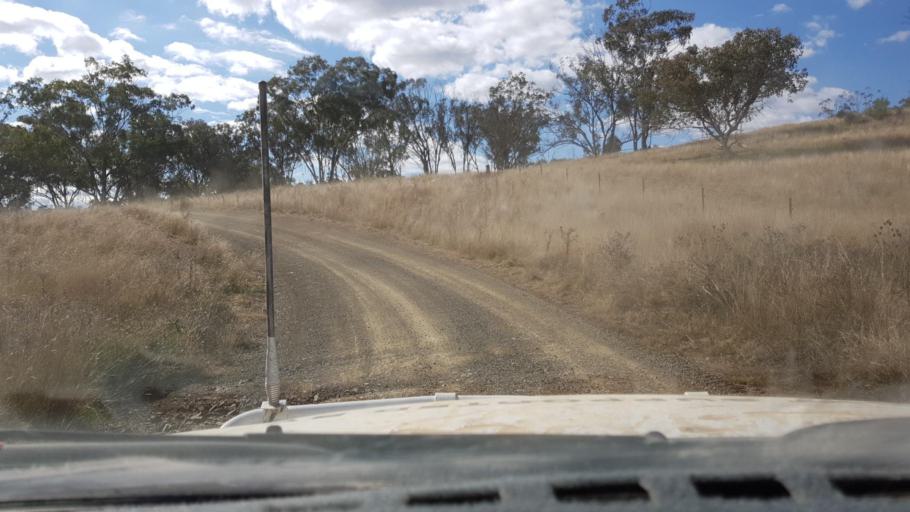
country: AU
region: New South Wales
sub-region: Tamworth Municipality
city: Manilla
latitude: -30.4618
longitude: 150.7801
